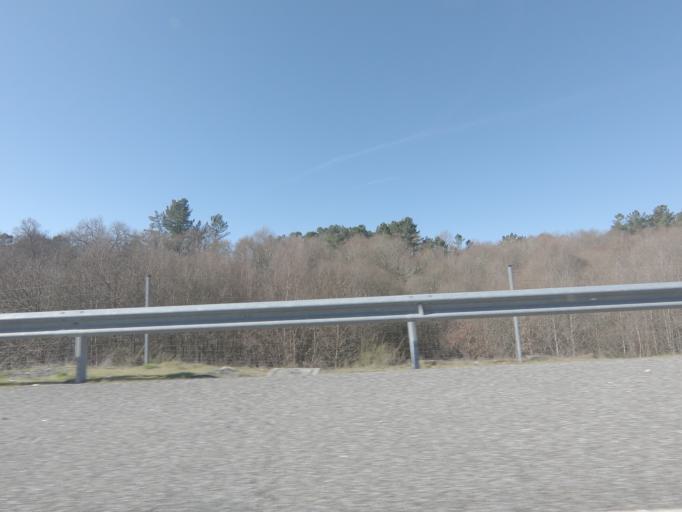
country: ES
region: Galicia
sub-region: Provincia de Ourense
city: Cea
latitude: 42.4673
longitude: -8.0278
